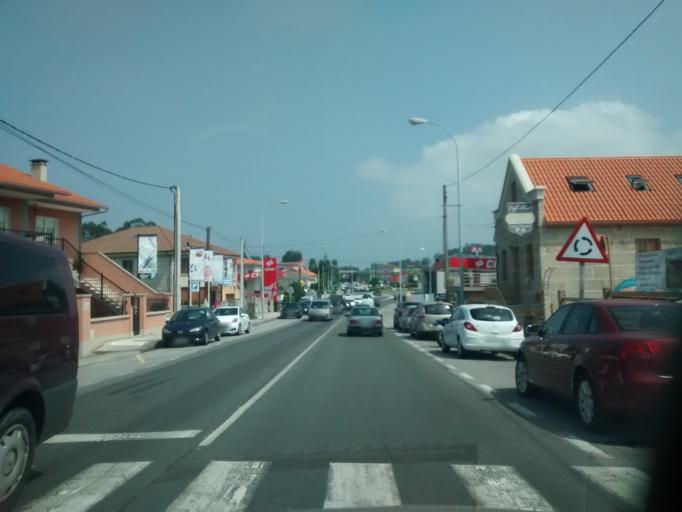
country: ES
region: Galicia
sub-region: Provincia de Pontevedra
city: Sanxenxo
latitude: 42.4104
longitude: -8.8132
